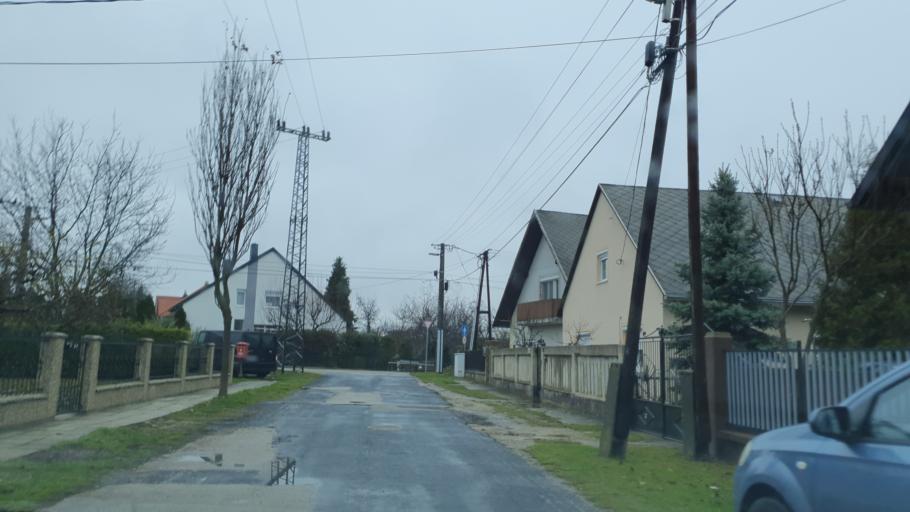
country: HU
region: Veszprem
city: Veszprem
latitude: 47.1394
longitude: 17.9441
